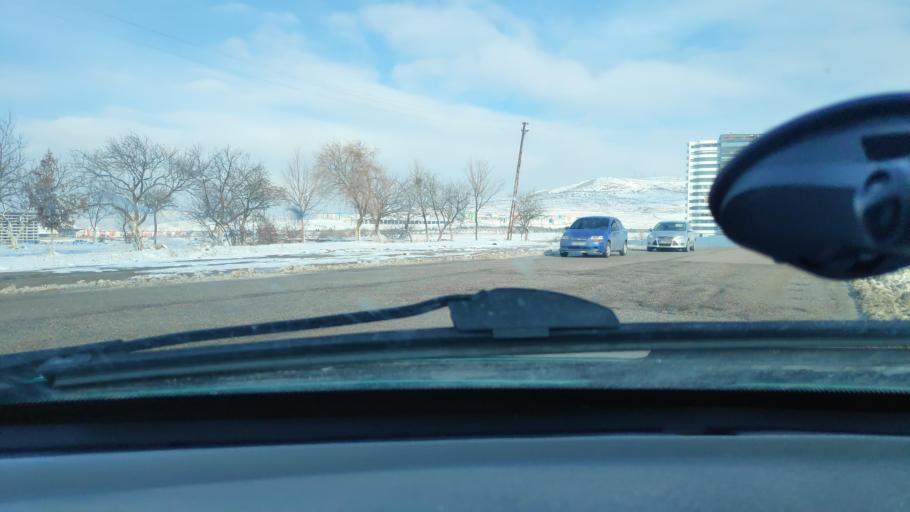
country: TR
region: Ankara
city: Ankara
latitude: 40.0142
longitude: 32.8371
